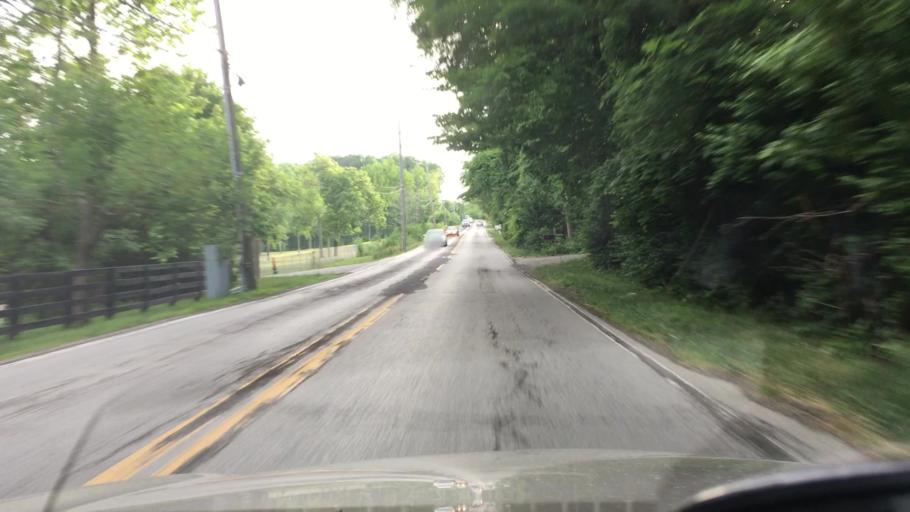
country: US
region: Indiana
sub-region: Marion County
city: Lawrence
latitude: 39.8800
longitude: -86.0160
